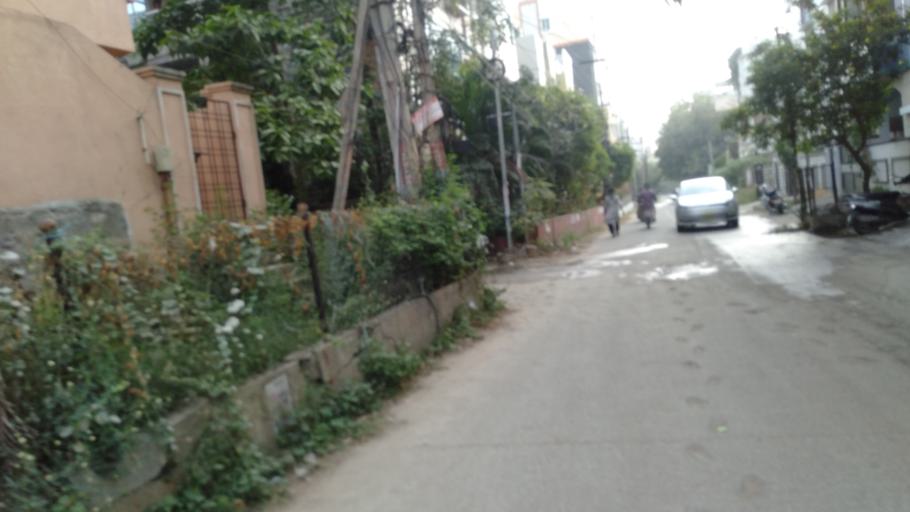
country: IN
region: Telangana
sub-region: Rangareddi
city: Kukatpalli
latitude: 17.4912
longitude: 78.3855
